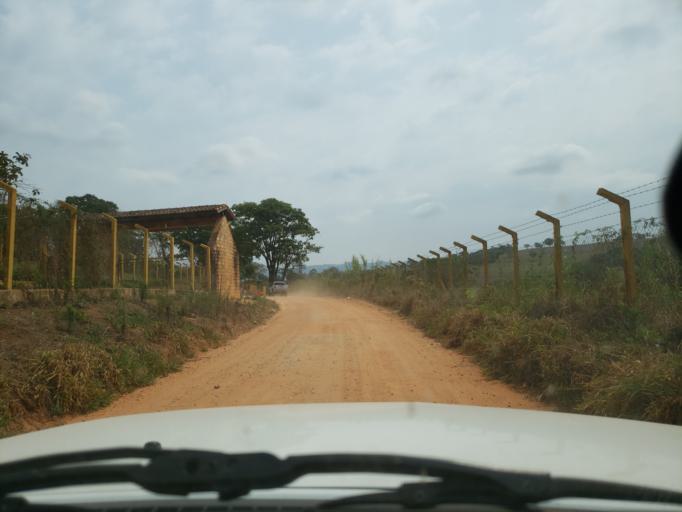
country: BR
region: Minas Gerais
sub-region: Jacutinga
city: Jacutinga
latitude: -22.3126
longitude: -46.6039
